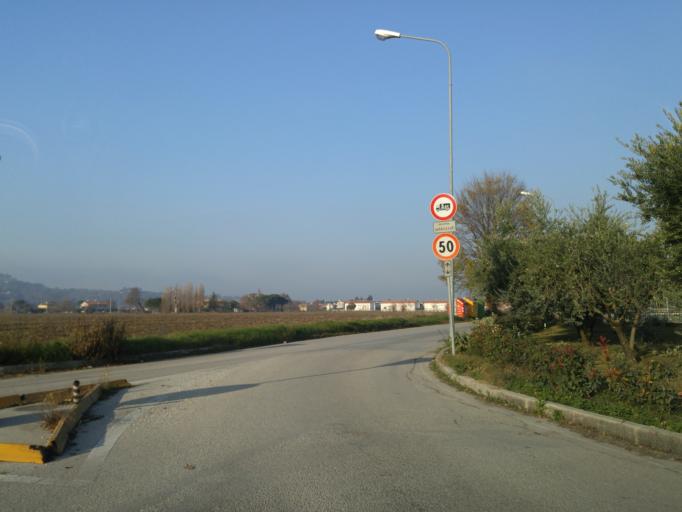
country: IT
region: The Marches
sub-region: Provincia di Pesaro e Urbino
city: Bellocchi
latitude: 43.7924
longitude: 12.9915
